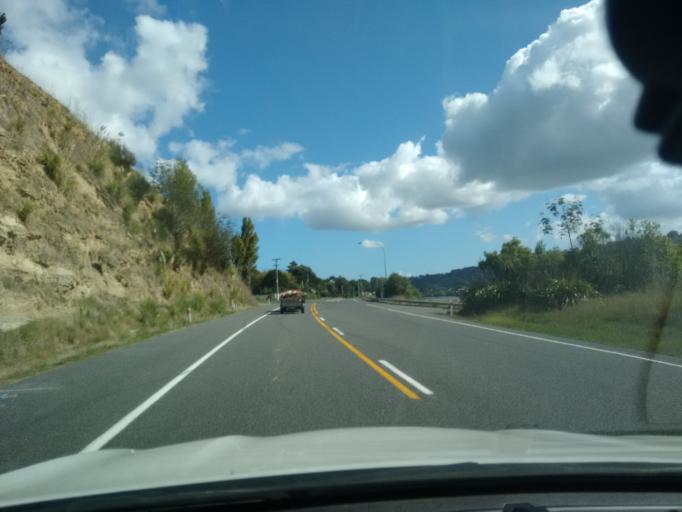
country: NZ
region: Manawatu-Wanganui
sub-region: Wanganui District
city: Wanganui
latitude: -39.8973
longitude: 175.0913
